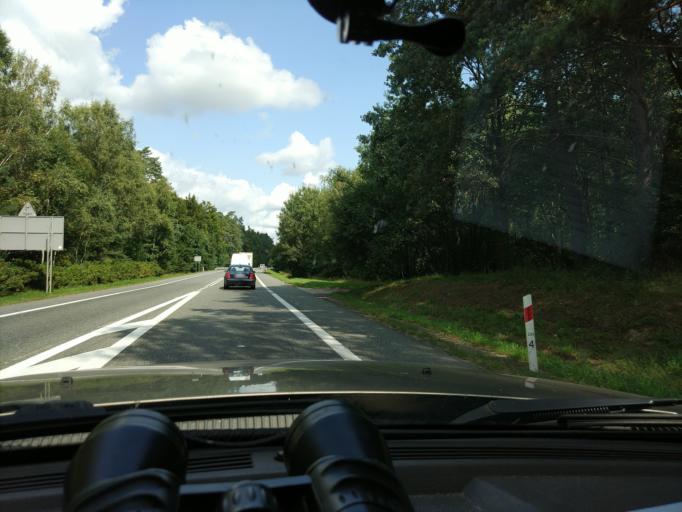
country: PL
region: Masovian Voivodeship
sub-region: Powiat mlawski
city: Mlawa
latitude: 53.1343
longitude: 20.3960
